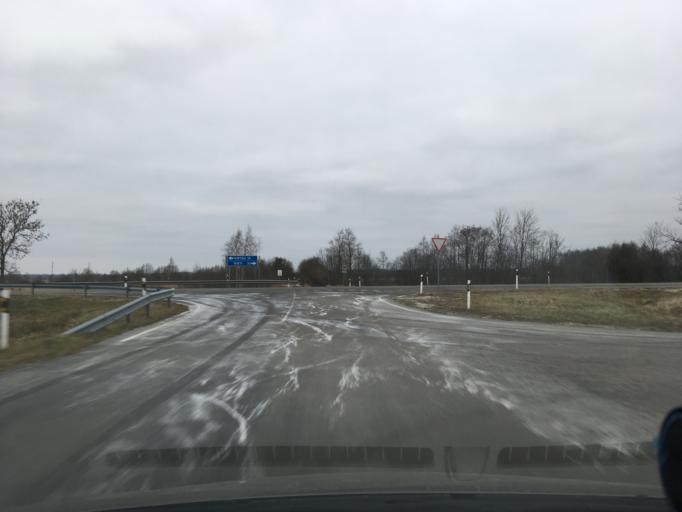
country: EE
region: Laeaene
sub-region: Lihula vald
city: Lihula
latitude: 58.7321
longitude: 23.9847
